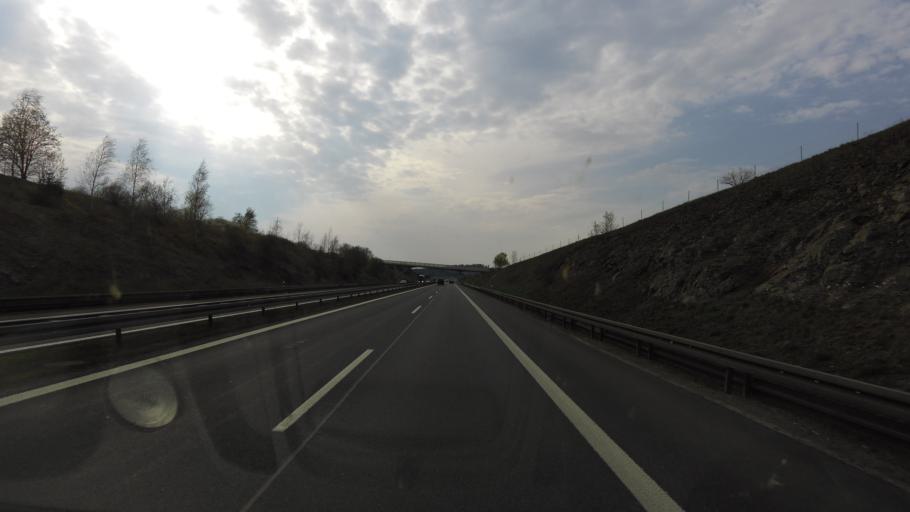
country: DE
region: Bavaria
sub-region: Upper Franconia
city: Gattendorf
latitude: 50.3462
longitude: 11.9888
